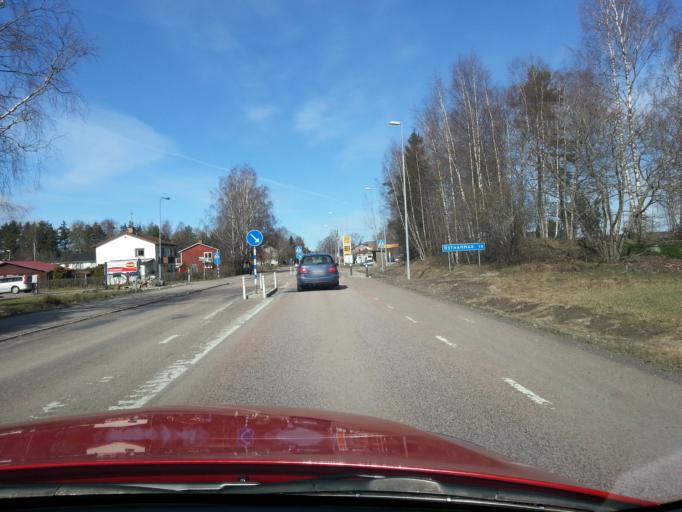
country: SE
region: Uppsala
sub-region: Osthammars Kommun
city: Gimo
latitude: 60.1670
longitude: 18.1936
